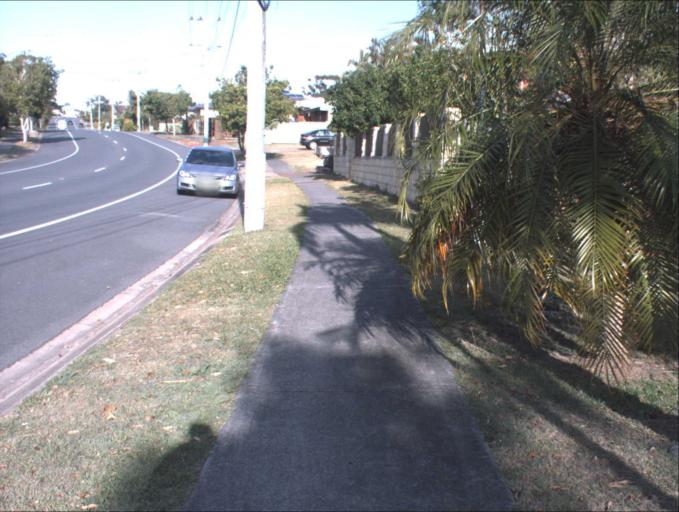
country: AU
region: Queensland
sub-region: Logan
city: Slacks Creek
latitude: -27.6517
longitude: 153.1792
